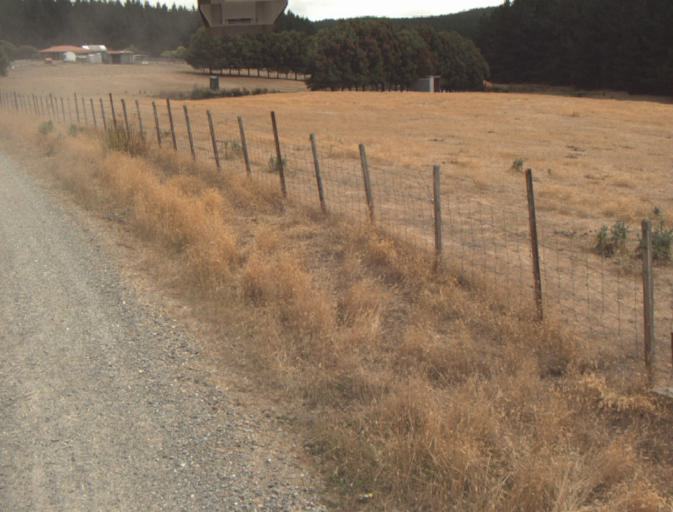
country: AU
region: Tasmania
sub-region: Launceston
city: Mayfield
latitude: -41.1534
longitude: 147.1805
